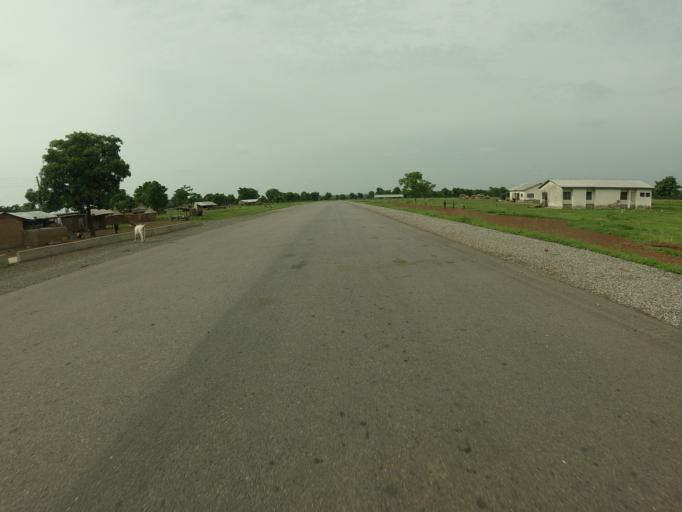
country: GH
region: Northern
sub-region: Yendi
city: Yendi
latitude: 9.8095
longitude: -0.1145
